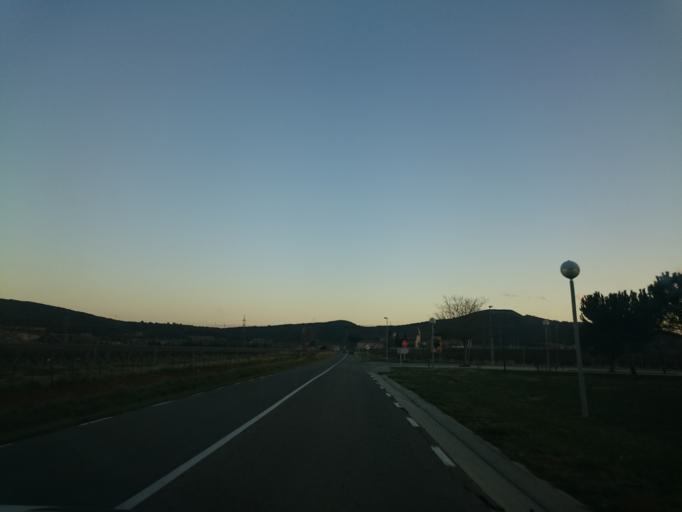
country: ES
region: Catalonia
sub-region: Provincia de Barcelona
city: La Granada
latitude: 41.3457
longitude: 1.7431
